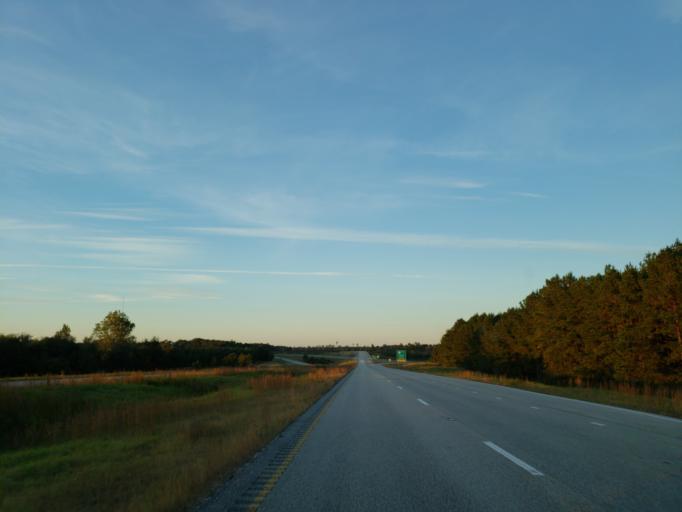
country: US
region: Mississippi
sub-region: Wayne County
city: Belmont
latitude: 31.4478
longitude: -88.4648
